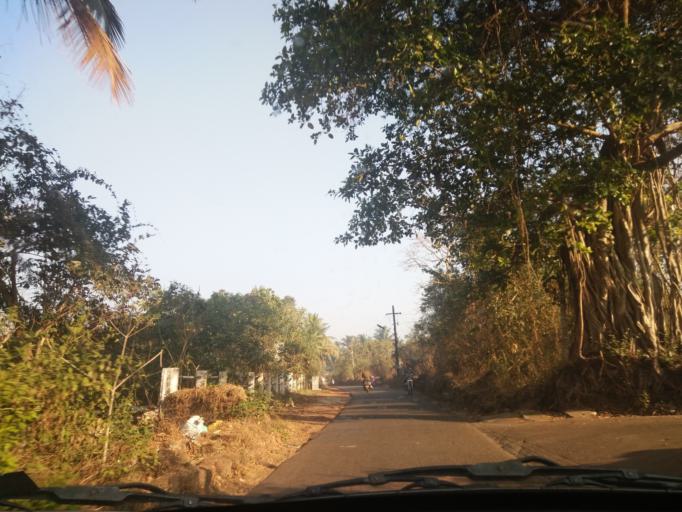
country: IN
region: Goa
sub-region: South Goa
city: Davorlim
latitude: 15.2840
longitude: 74.0068
